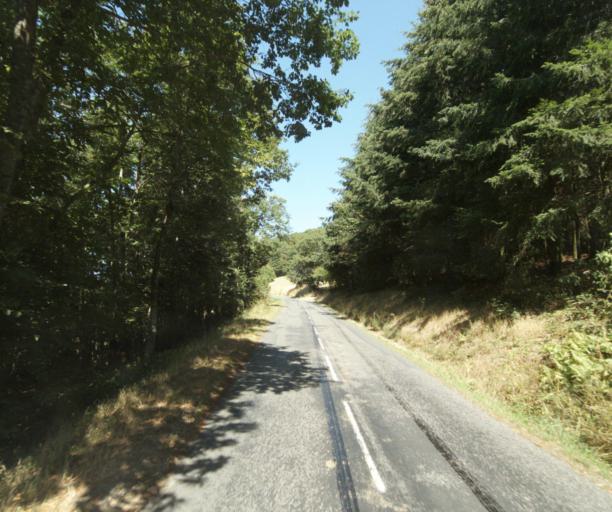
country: FR
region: Rhone-Alpes
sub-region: Departement du Rhone
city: Courzieu
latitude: 45.7209
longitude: 4.5499
